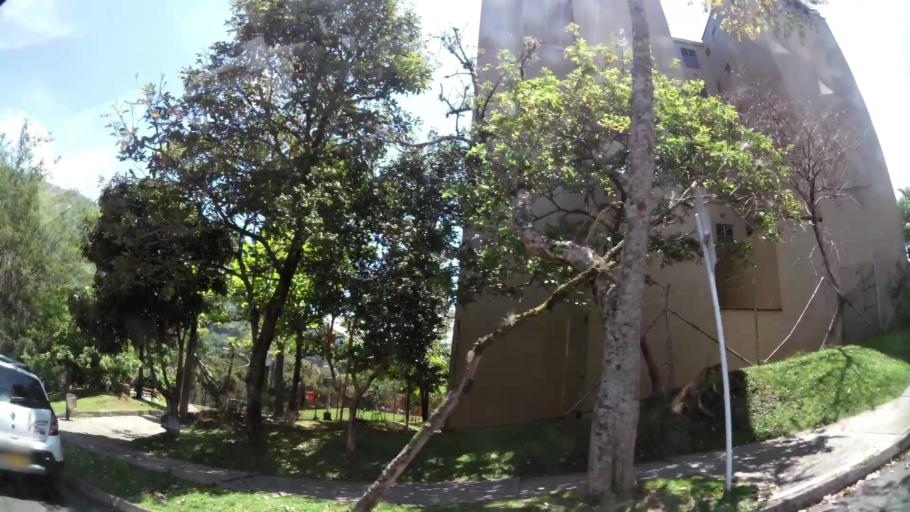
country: CO
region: Antioquia
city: La Estrella
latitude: 6.1860
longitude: -75.6441
